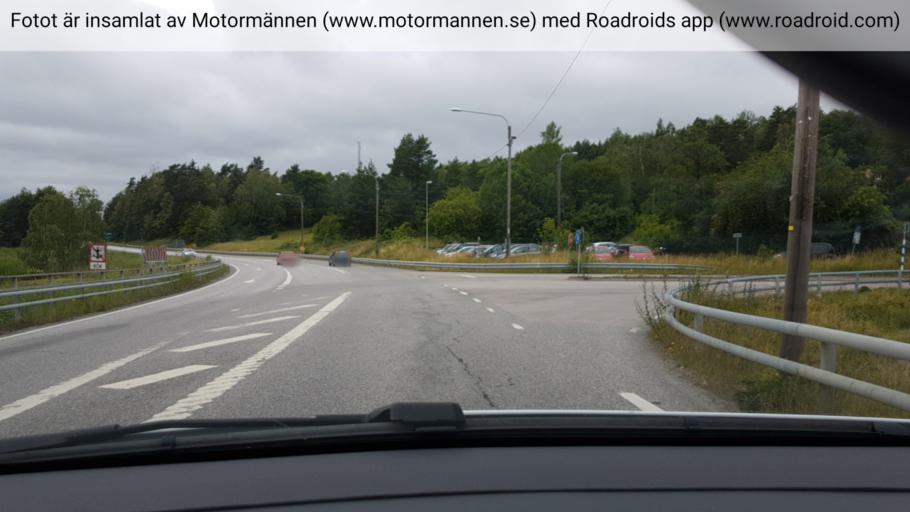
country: SE
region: Stockholm
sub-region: Vaxholms Kommun
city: Resaro
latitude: 59.4171
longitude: 18.3104
